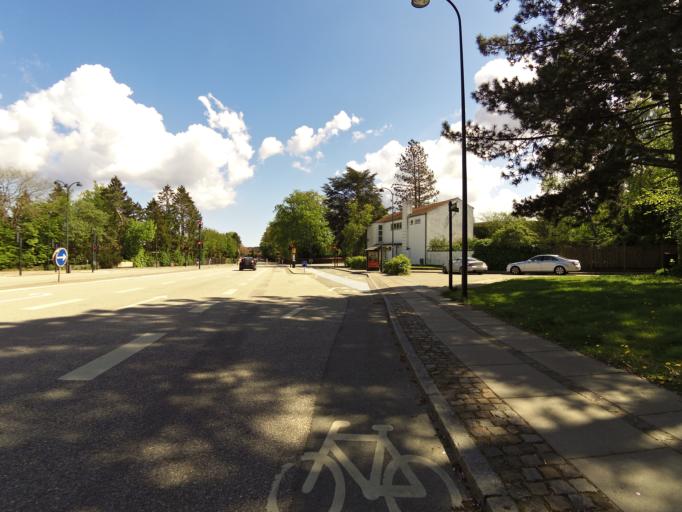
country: DK
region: Capital Region
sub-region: Gentofte Kommune
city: Charlottenlund
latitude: 55.7367
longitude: 12.5493
